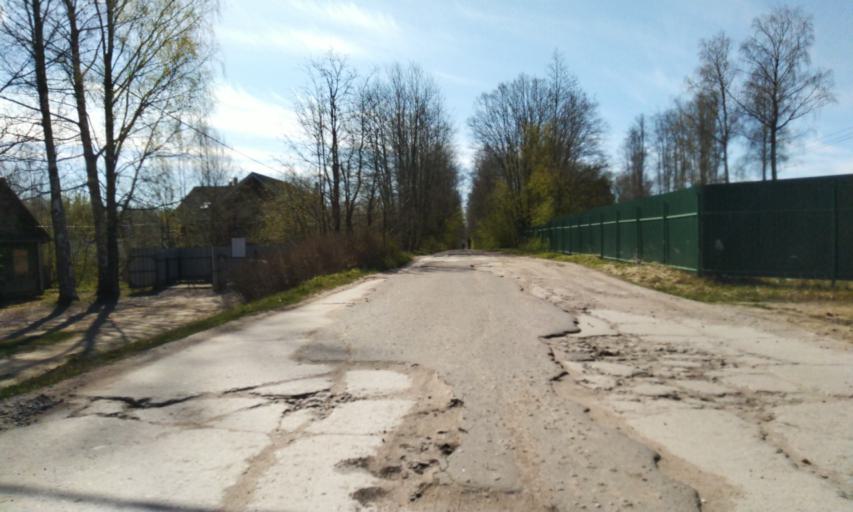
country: RU
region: Leningrad
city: Garbolovo
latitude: 60.3894
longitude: 30.4814
